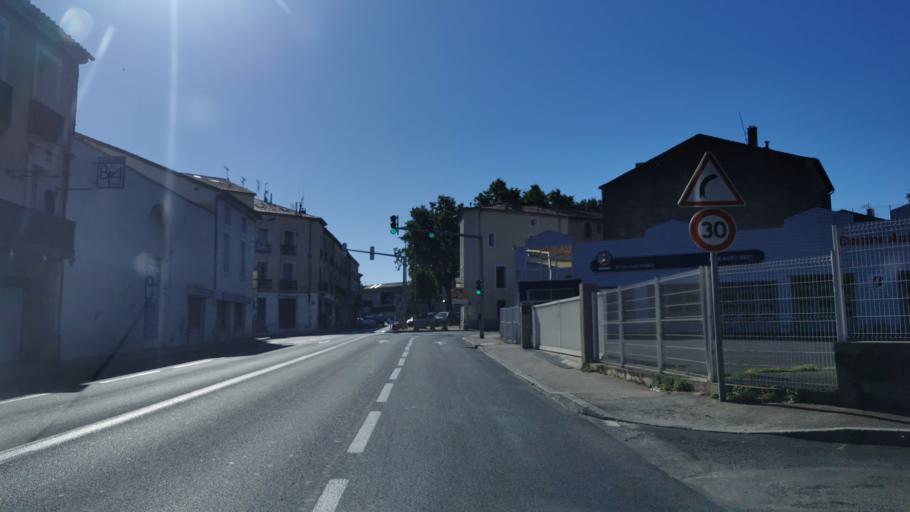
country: FR
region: Languedoc-Roussillon
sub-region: Departement de l'Herault
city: Beziers
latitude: 43.3383
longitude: 3.2057
